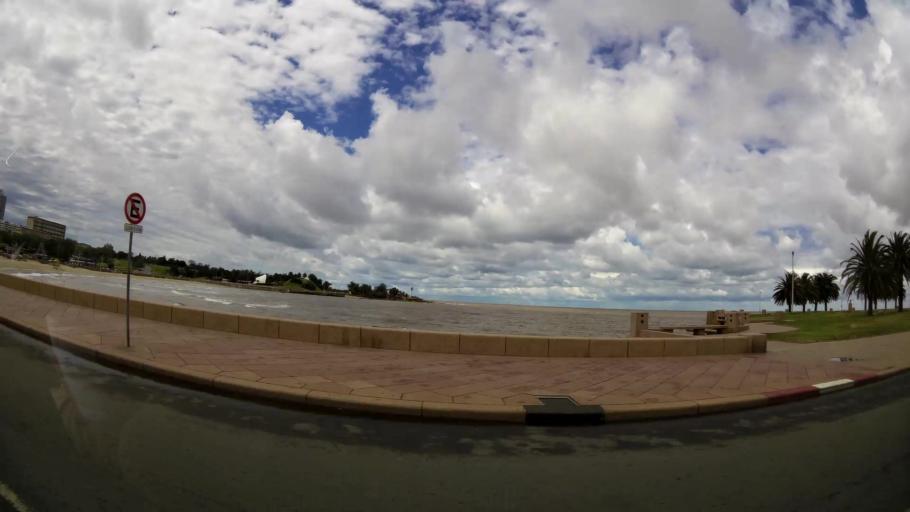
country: UY
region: Montevideo
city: Montevideo
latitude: -34.9146
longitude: -56.1718
